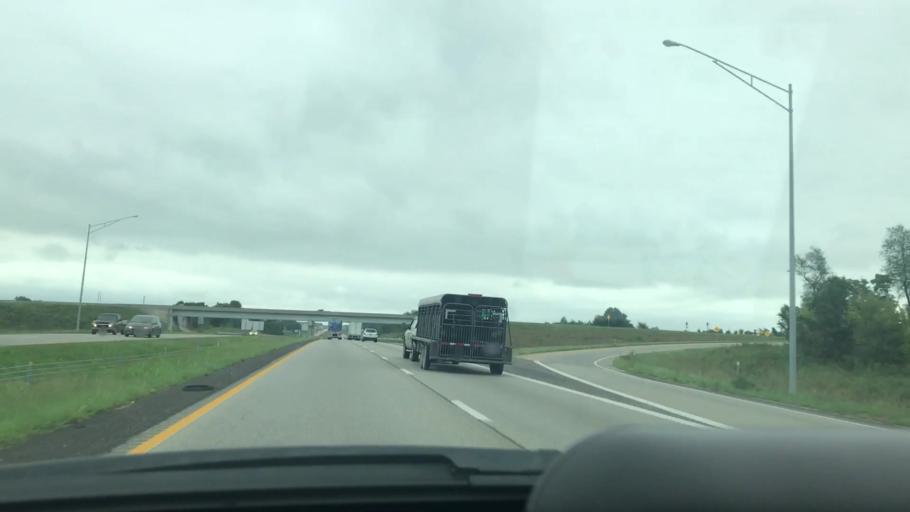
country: US
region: Missouri
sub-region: Greene County
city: Republic
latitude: 37.1954
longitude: -93.4474
